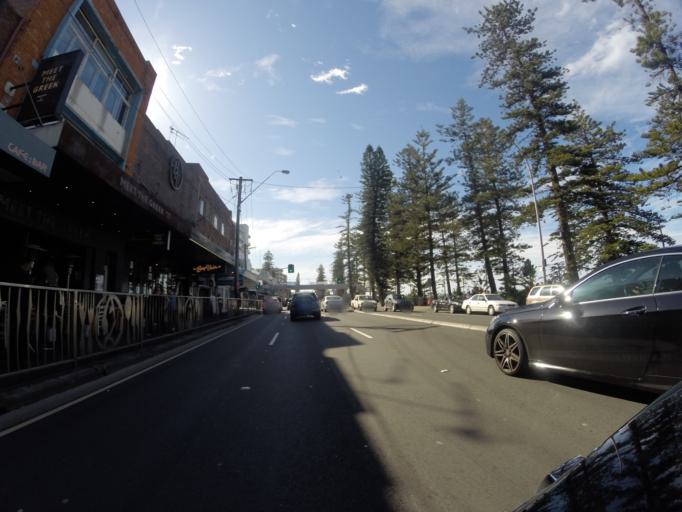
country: AU
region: New South Wales
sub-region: Rockdale
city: Brighton-Le-Sands
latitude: -33.9614
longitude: 151.1560
